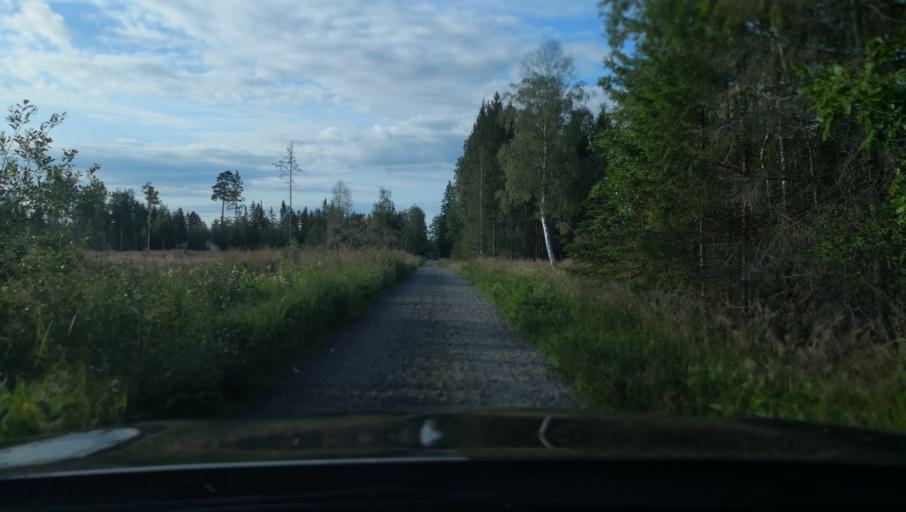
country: SE
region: Uppsala
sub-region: Osthammars Kommun
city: Osterbybruk
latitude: 60.0352
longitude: 17.9193
